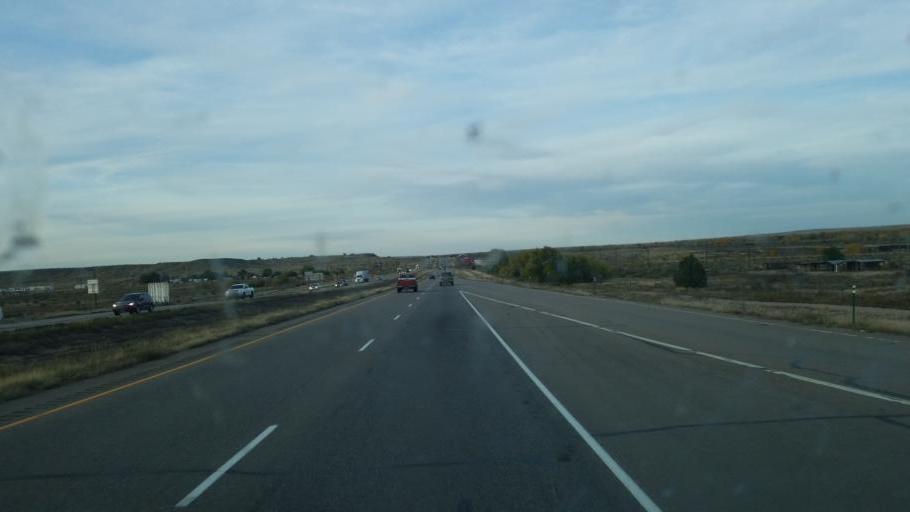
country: US
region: Colorado
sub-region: Pueblo County
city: Pueblo West
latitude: 38.4036
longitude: -104.6160
